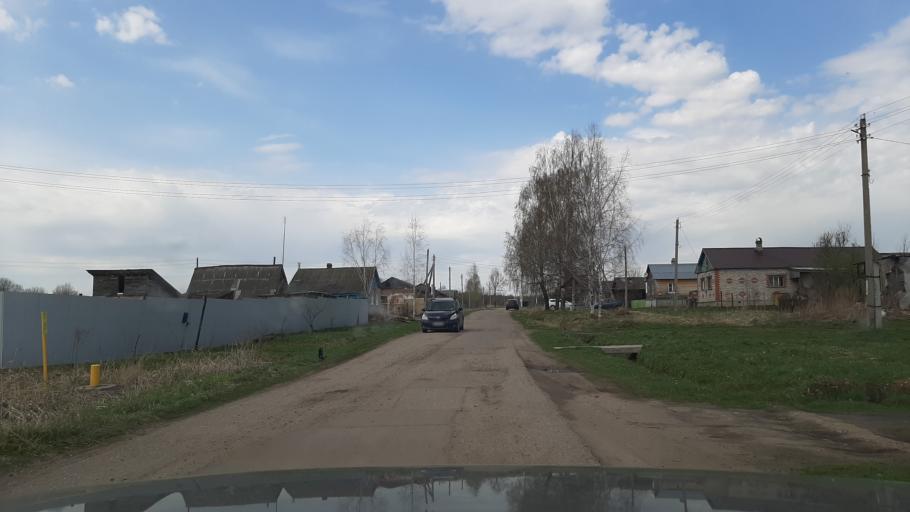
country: RU
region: Ivanovo
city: Furmanov
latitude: 57.3183
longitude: 41.1593
